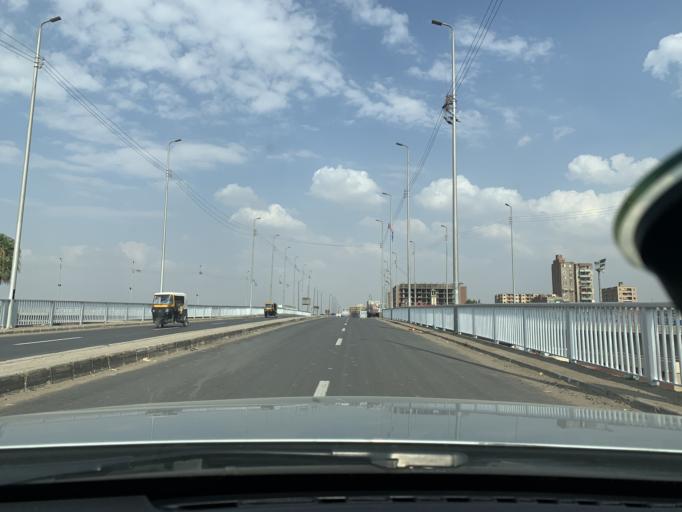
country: EG
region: Muhafazat al Qahirah
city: Cairo
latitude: 30.1308
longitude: 31.2884
